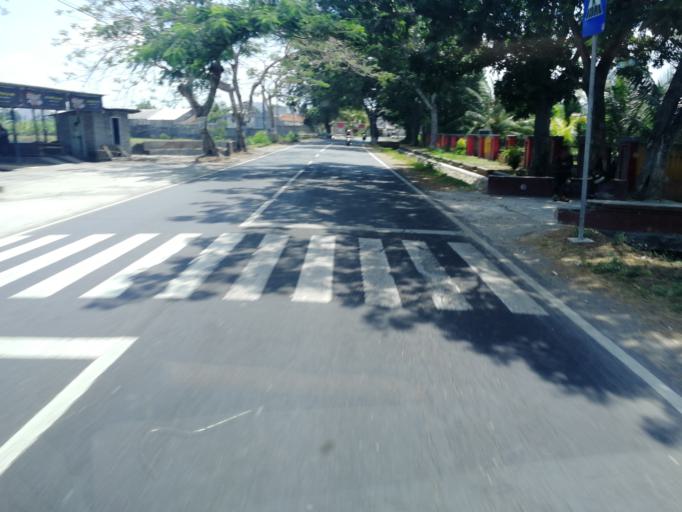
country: ID
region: West Nusa Tenggara
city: Jelateng Timur
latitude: -8.7055
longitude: 116.0869
